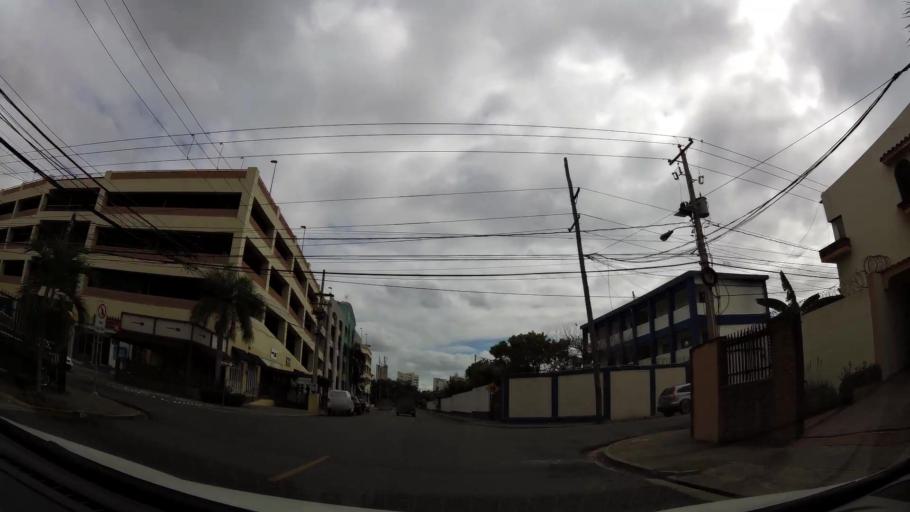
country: DO
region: Nacional
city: Bella Vista
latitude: 18.4524
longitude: -69.9423
